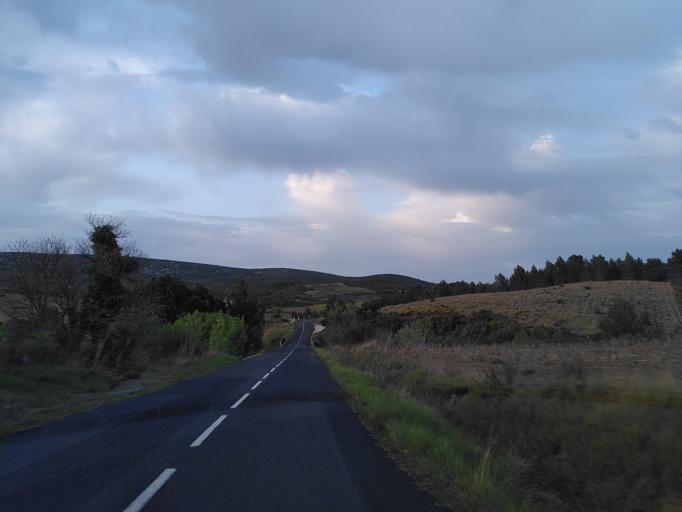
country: FR
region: Languedoc-Roussillon
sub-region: Departement des Pyrenees-Orientales
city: Estagel
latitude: 42.8125
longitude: 2.6986
